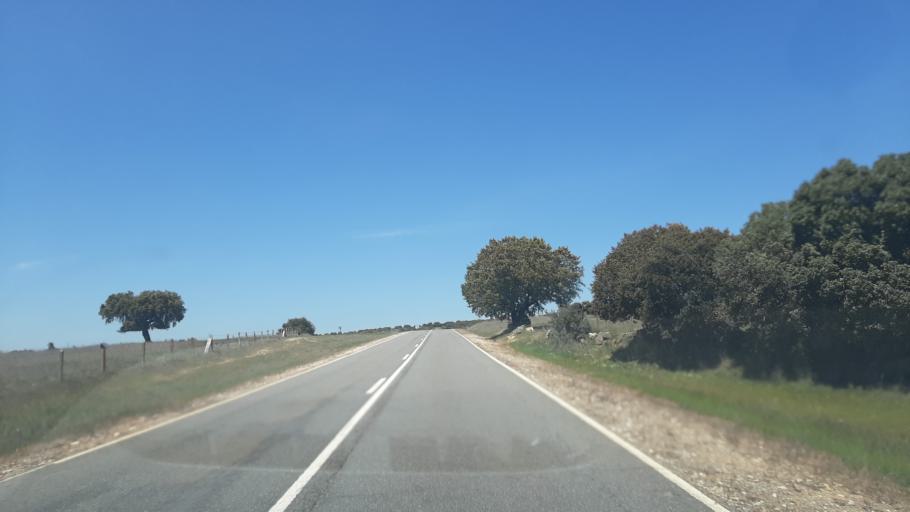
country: ES
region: Castille and Leon
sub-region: Provincia de Salamanca
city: Puente del Congosto
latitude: 40.5246
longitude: -5.5030
